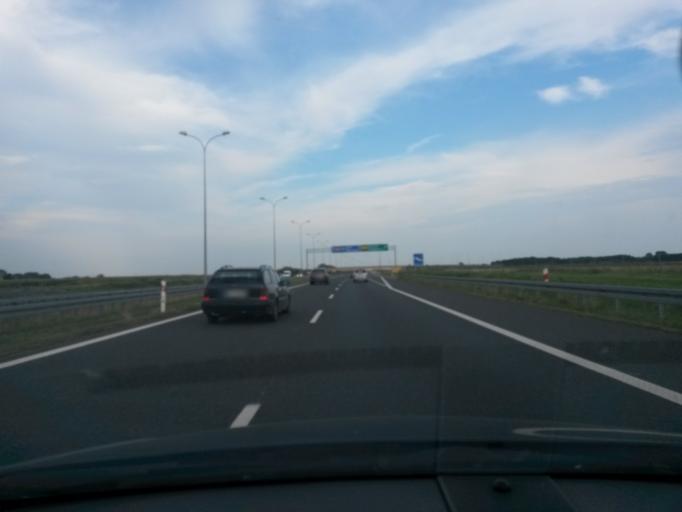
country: PL
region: Lodz Voivodeship
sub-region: Powiat poddebicki
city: Wartkowice
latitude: 51.9961
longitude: 19.0319
